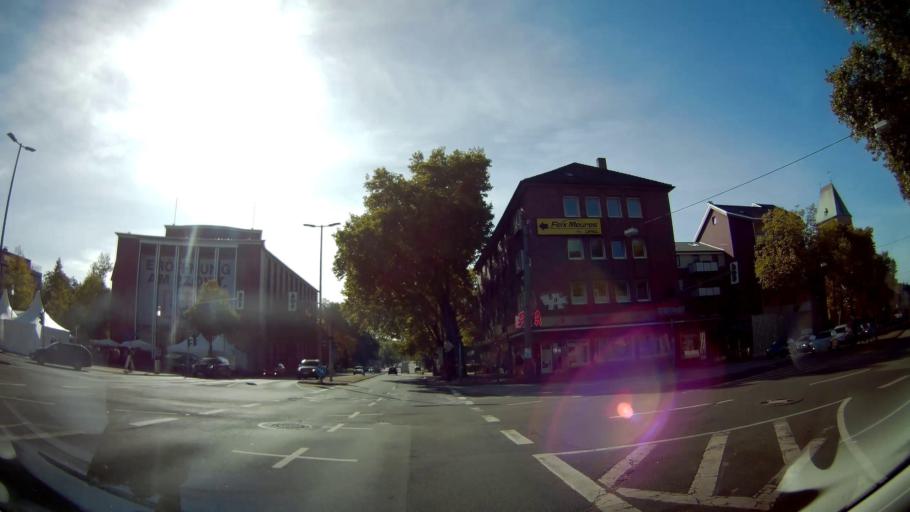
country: DE
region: North Rhine-Westphalia
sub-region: Regierungsbezirk Arnsberg
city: Bochum
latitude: 51.4732
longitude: 7.2162
